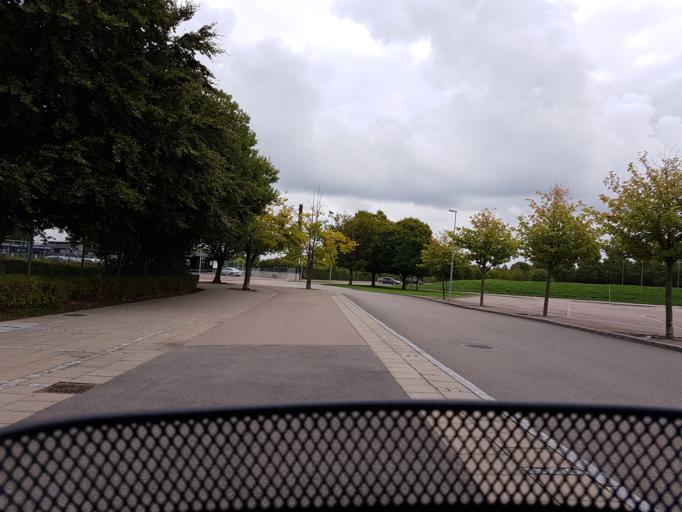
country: SE
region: Skane
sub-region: Landskrona
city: Landskrona
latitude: 55.8889
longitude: 12.8370
